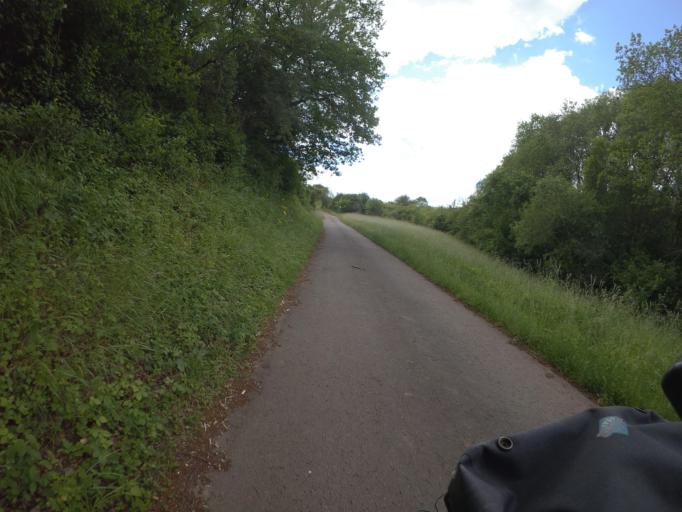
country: DE
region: Rheinland-Pfalz
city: Oberndorf
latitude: 49.7136
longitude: 7.8075
